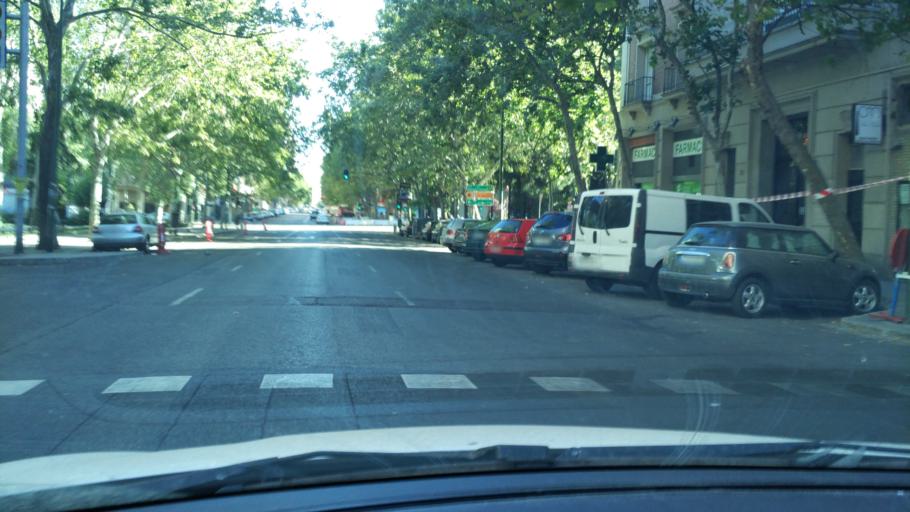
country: ES
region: Madrid
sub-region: Provincia de Madrid
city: Chamartin
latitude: 40.4533
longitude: -3.6949
